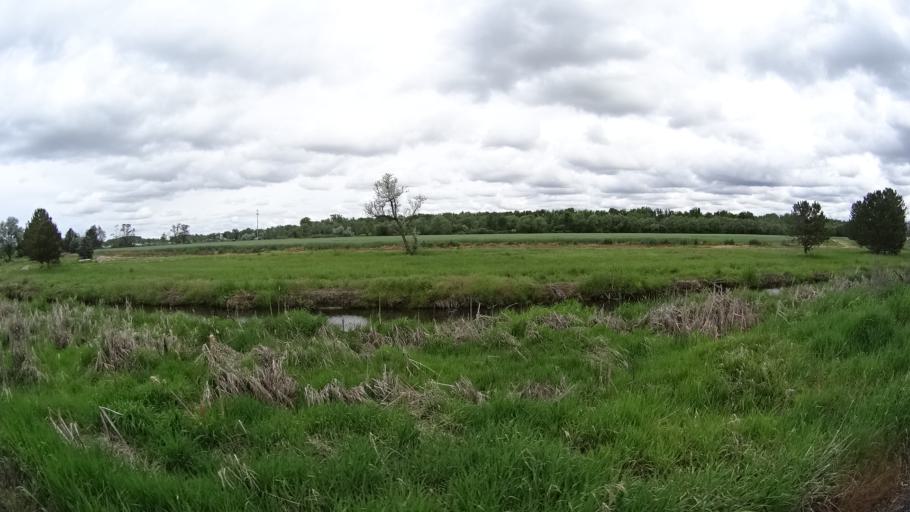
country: US
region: Idaho
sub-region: Ada County
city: Eagle
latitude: 43.6842
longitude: -116.3801
